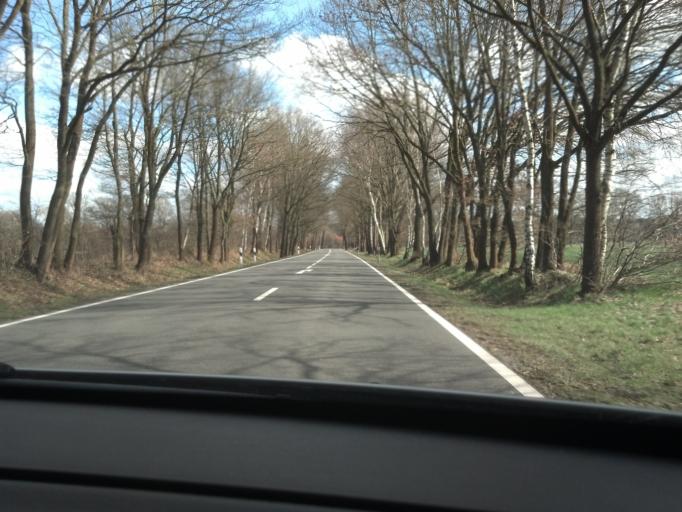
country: DE
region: Schleswig-Holstein
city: Langenlehsten
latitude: 53.4463
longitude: 10.7619
